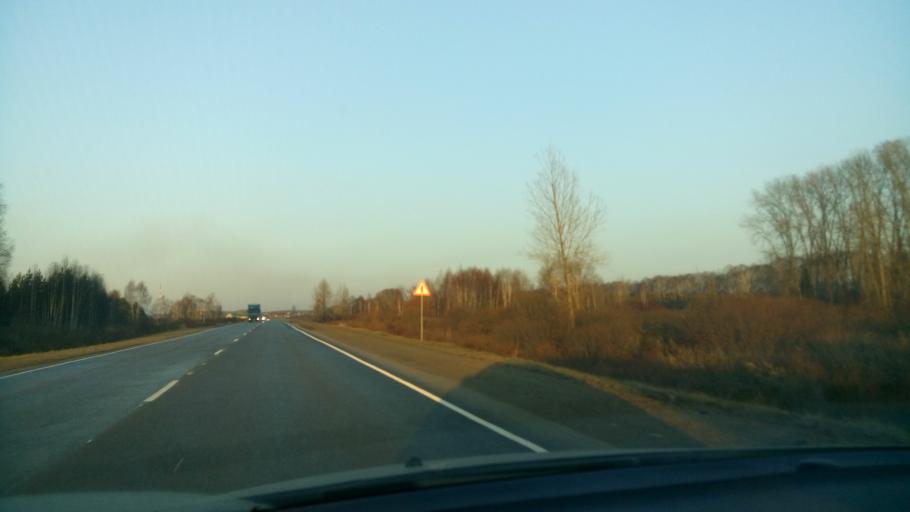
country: RU
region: Sverdlovsk
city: Obukhovskoye
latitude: 56.8331
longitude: 62.5695
